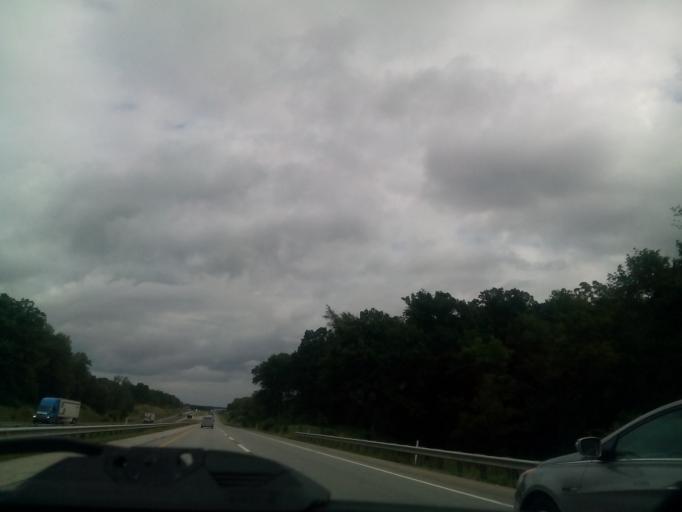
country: US
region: Indiana
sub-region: Steuben County
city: Fremont
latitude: 41.7099
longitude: -84.9389
